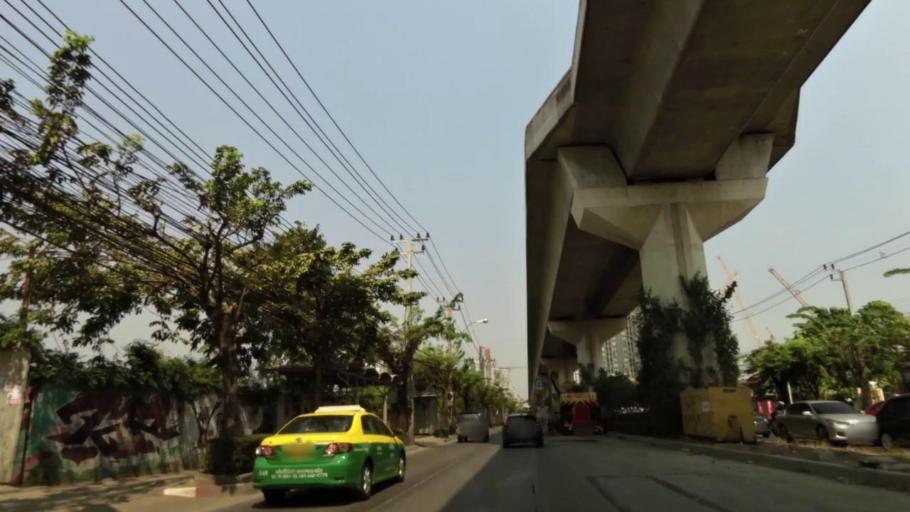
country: TH
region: Bangkok
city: Phra Khanong
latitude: 13.6628
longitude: 100.6024
